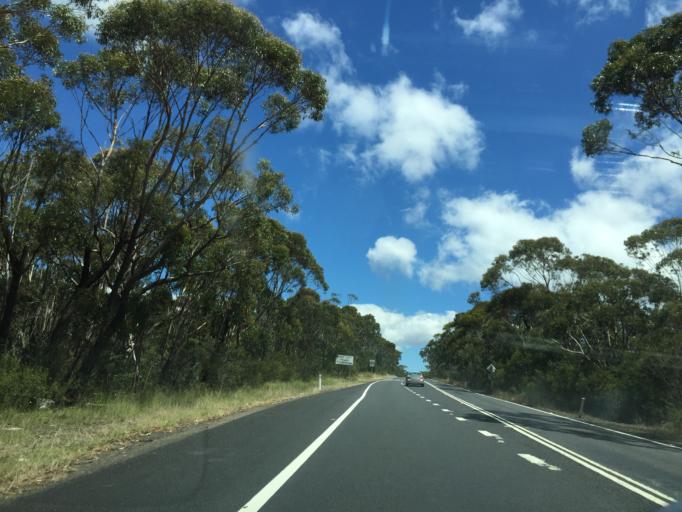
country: AU
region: New South Wales
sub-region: Blue Mountains Municipality
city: Blackheath
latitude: -33.5662
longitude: 150.3639
